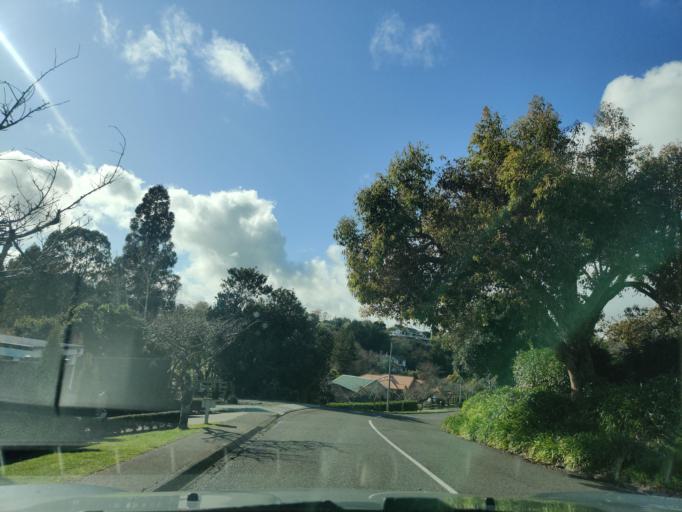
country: NZ
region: Hawke's Bay
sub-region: Hastings District
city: Hastings
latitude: -39.6743
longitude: 176.8916
